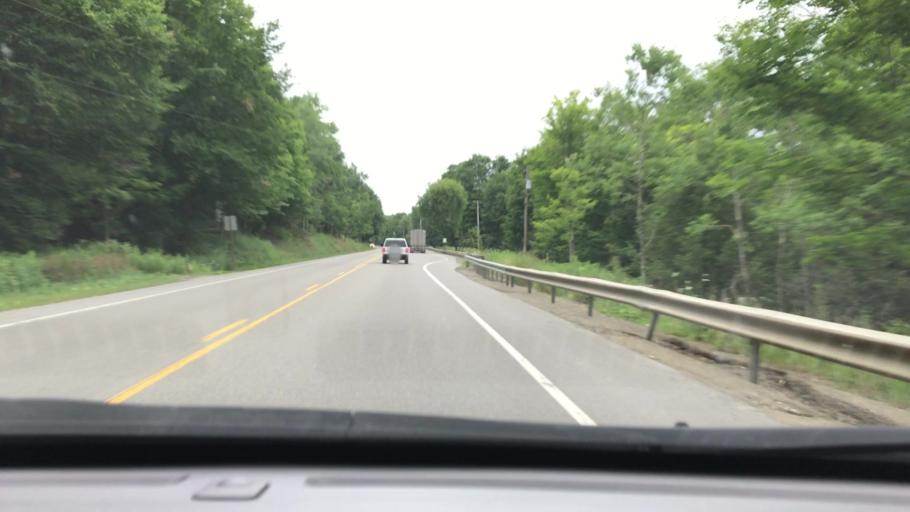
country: US
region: Pennsylvania
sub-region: McKean County
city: Kane
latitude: 41.6978
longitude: -78.6914
